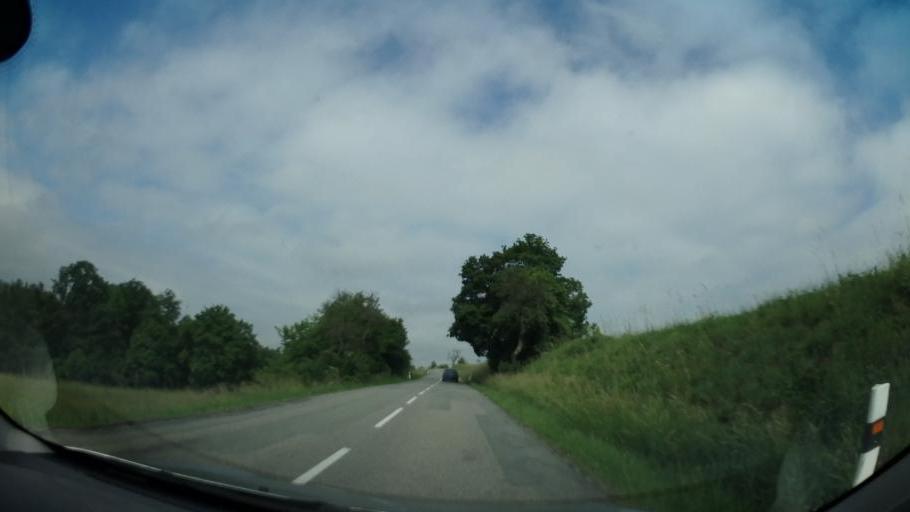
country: CZ
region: South Moravian
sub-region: Okres Brno-Venkov
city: Dolni Loucky
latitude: 49.3730
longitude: 16.3633
